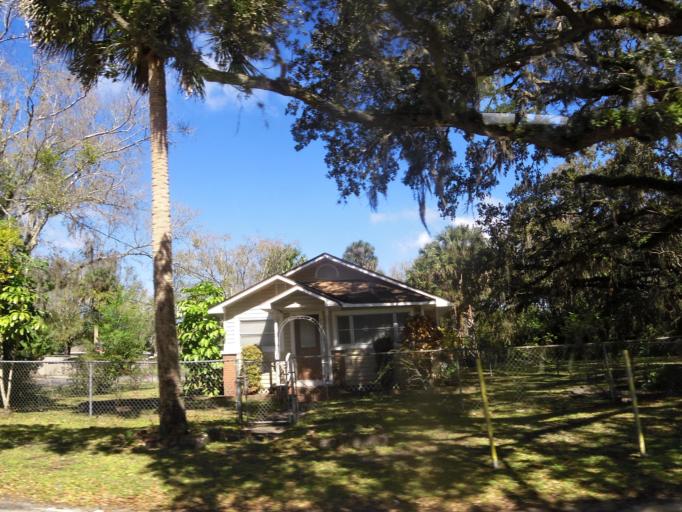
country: US
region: Florida
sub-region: Seminole County
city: Sanford
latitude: 28.8053
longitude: -81.2801
